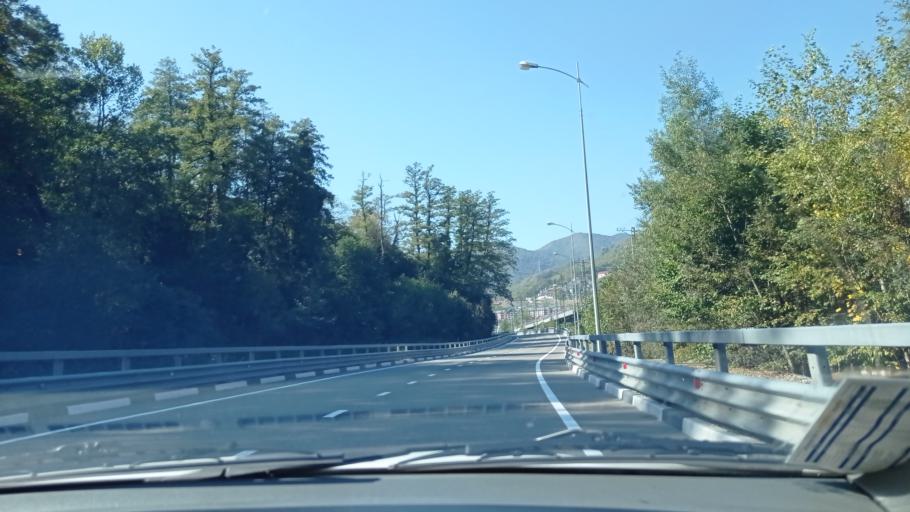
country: RU
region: Krasnodarskiy
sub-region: Sochi City
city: Krasnaya Polyana
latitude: 43.6836
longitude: 40.2403
